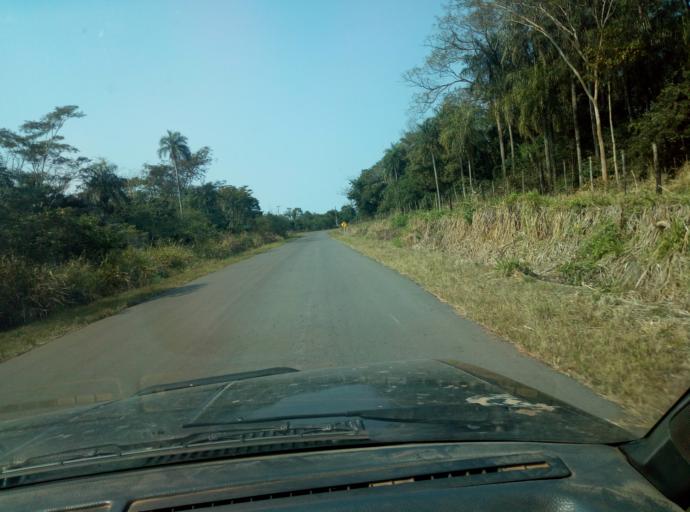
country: PY
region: Caaguazu
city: Carayao
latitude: -25.2047
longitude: -56.3072
